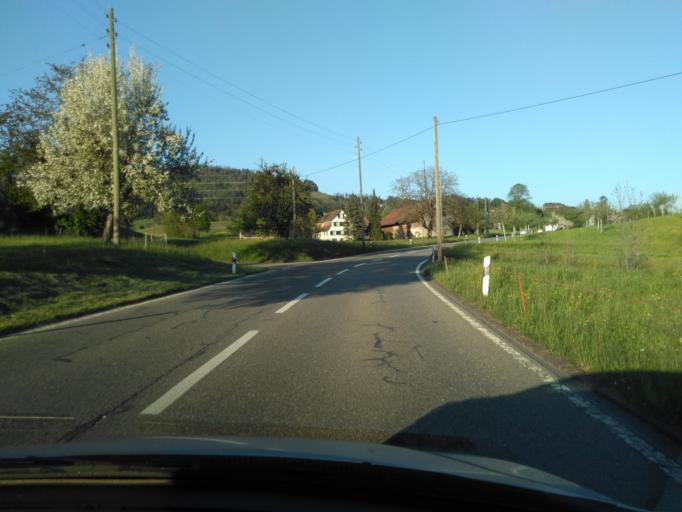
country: CH
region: Zurich
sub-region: Bezirk Hinwil
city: Tann
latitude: 47.2779
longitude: 8.8532
